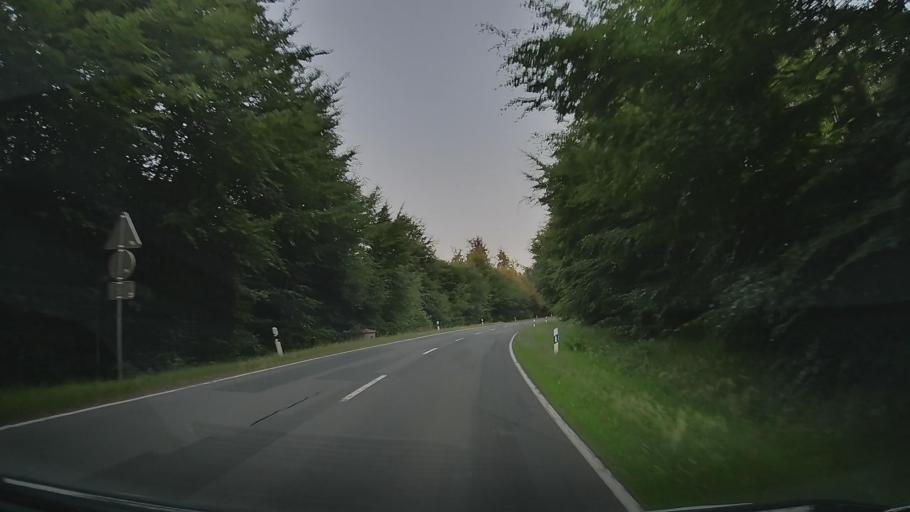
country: DE
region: Lower Saxony
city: Aerzen
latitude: 52.0251
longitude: 9.2834
